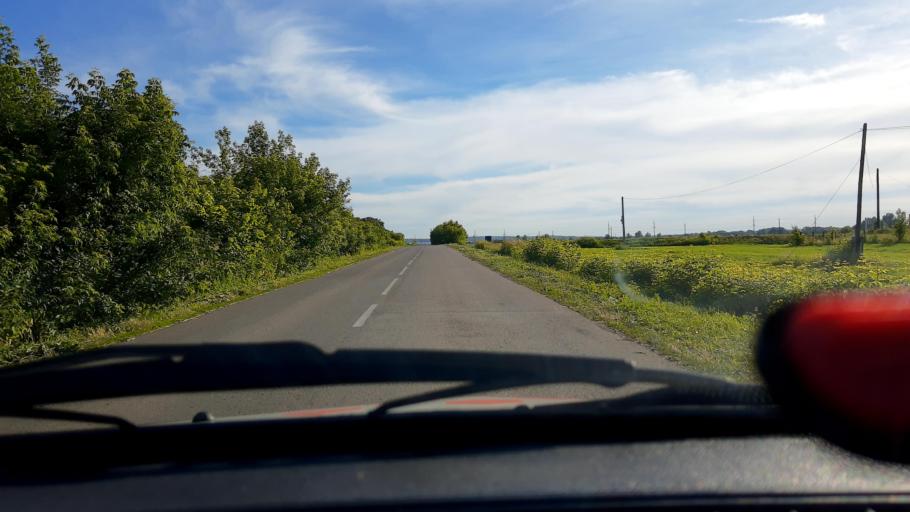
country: RU
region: Bashkortostan
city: Kabakovo
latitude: 54.5113
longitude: 55.9393
